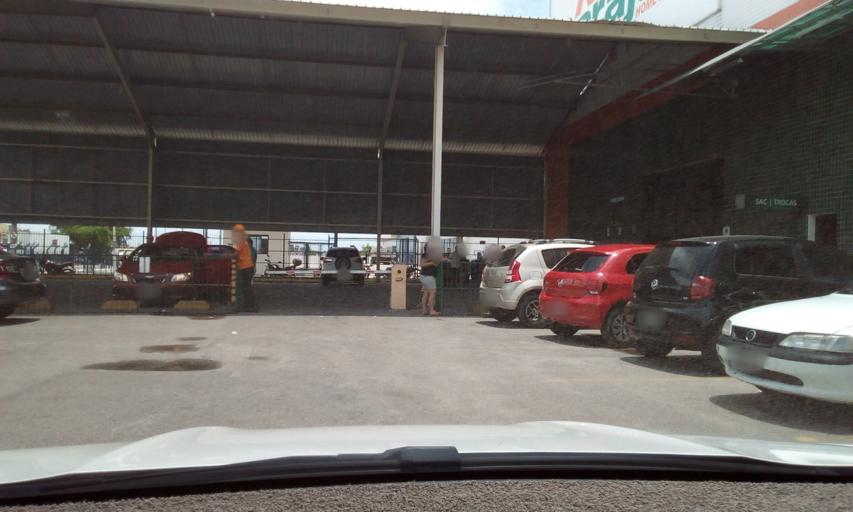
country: BR
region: Paraiba
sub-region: Joao Pessoa
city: Joao Pessoa
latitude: -7.1712
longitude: -34.8706
